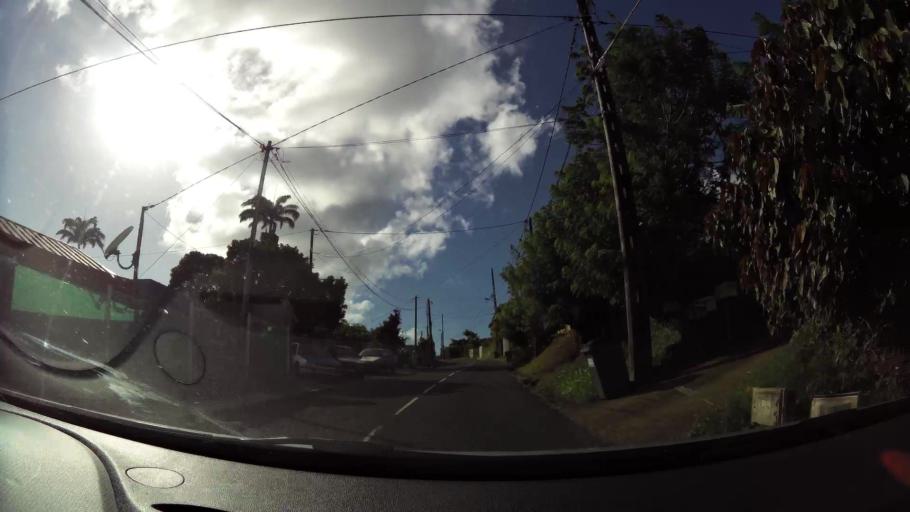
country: MQ
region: Martinique
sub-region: Martinique
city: Fort-de-France
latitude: 14.6497
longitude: -61.0815
